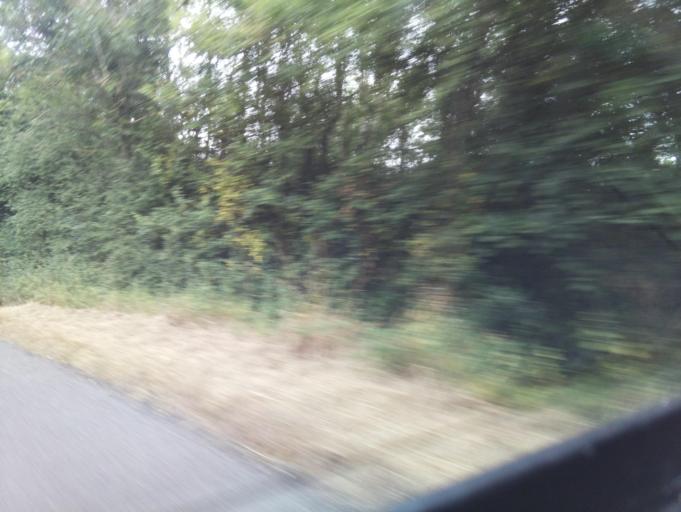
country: GB
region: England
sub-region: Leicestershire
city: Measham
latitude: 52.7265
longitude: -1.5096
